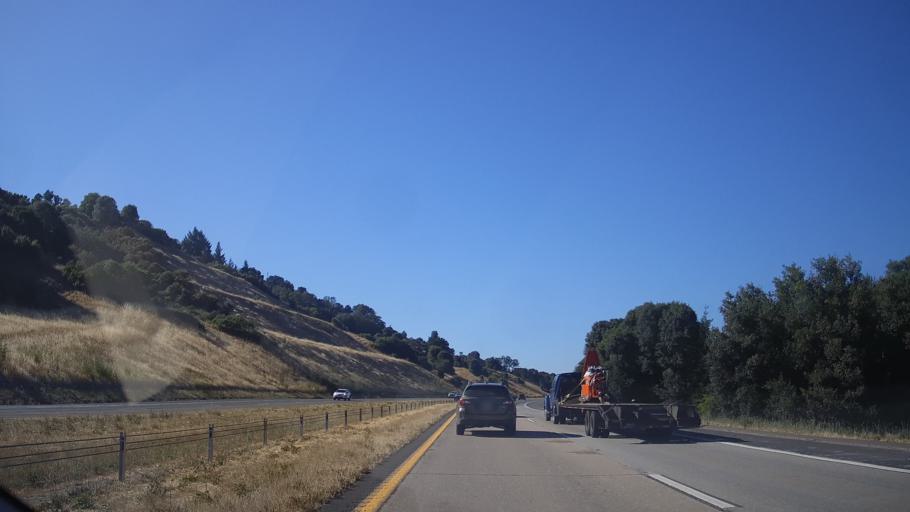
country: US
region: California
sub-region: Mendocino County
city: Redwood Valley
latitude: 39.2166
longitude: -123.2061
